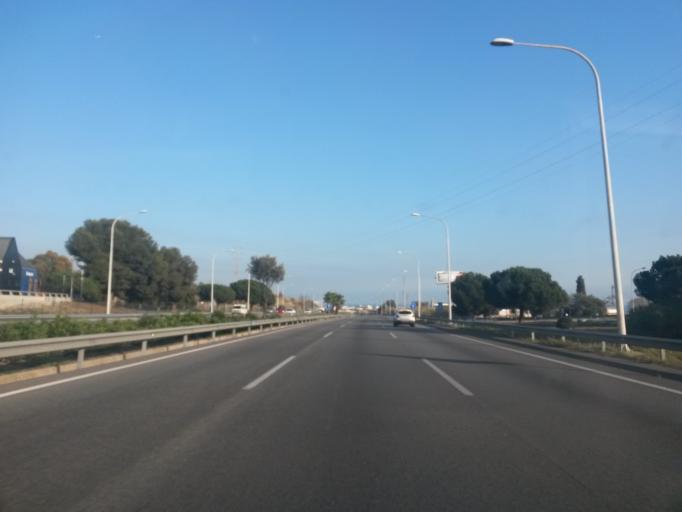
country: ES
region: Catalonia
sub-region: Provincia de Barcelona
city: Teia
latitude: 41.4925
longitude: 2.3331
